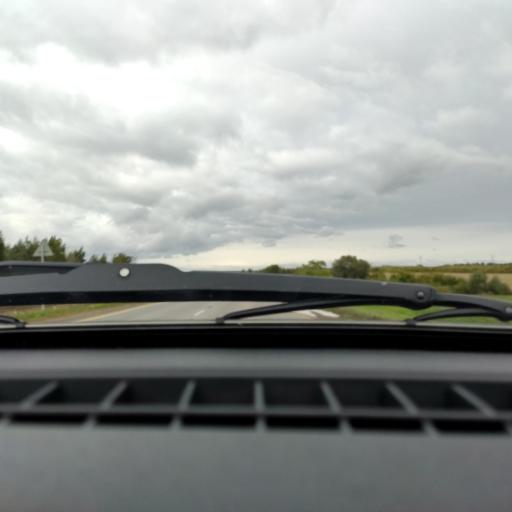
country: RU
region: Bashkortostan
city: Rayevskiy
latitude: 54.0906
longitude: 54.9116
